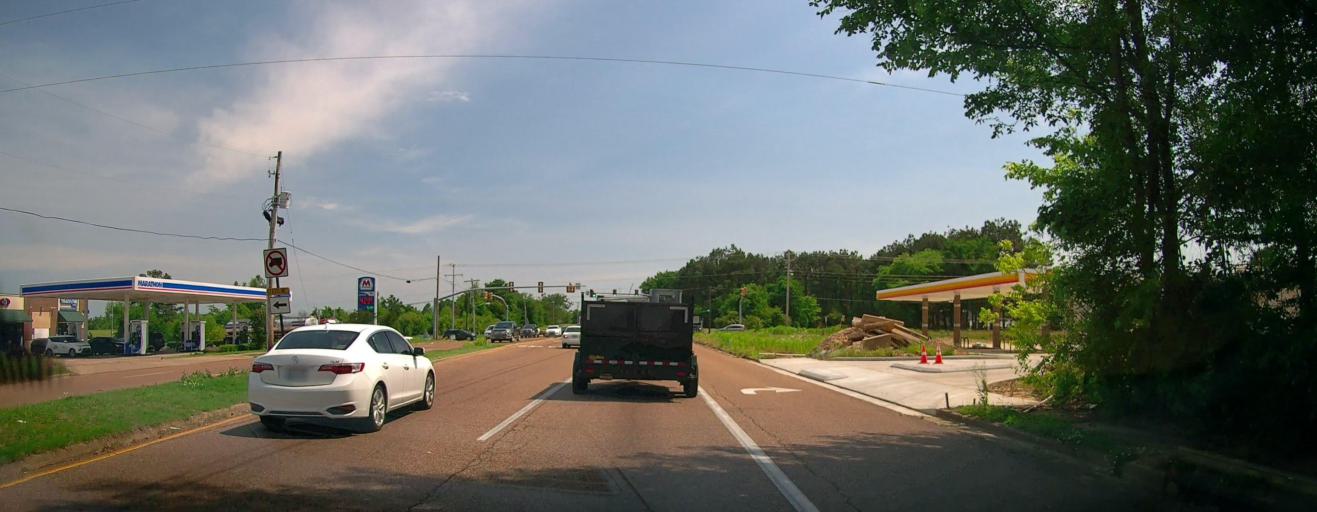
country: US
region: Mississippi
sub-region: De Soto County
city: Olive Branch
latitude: 34.9958
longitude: -89.8309
